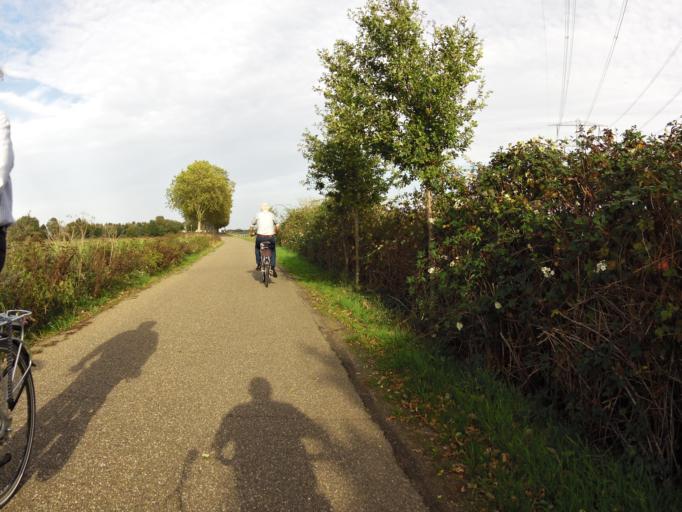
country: BE
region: Flanders
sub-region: Provincie Limburg
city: Maaseik
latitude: 51.1210
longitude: 5.8125
